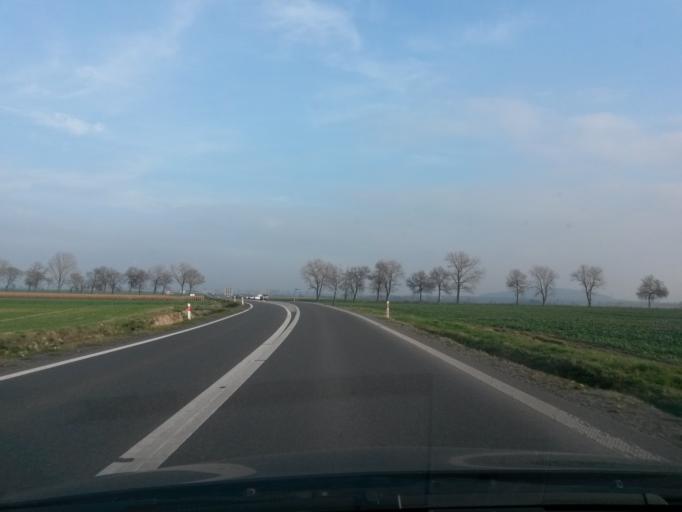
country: PL
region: Lower Silesian Voivodeship
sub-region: Powiat sredzki
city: Udanin
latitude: 50.9938
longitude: 16.4846
